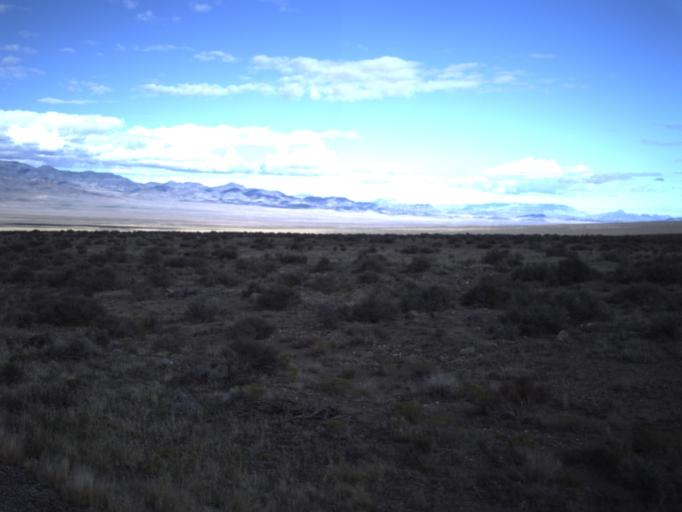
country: US
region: Utah
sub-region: Beaver County
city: Milford
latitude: 38.4437
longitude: -113.3251
